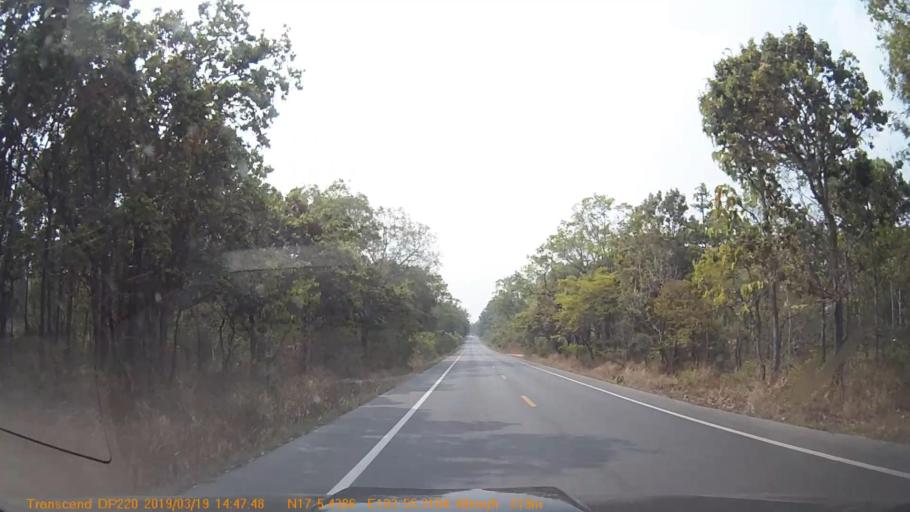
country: TH
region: Sakon Nakhon
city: Kut Bak
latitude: 17.0910
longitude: 103.9215
